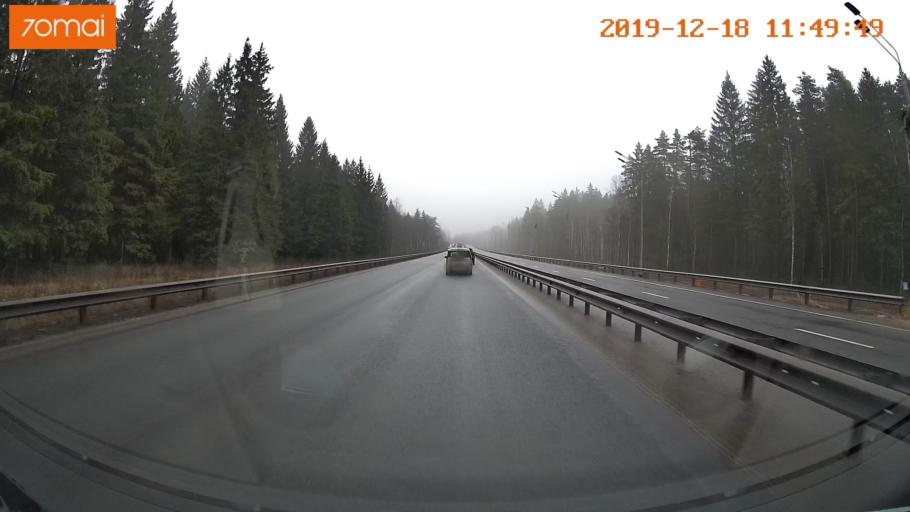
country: RU
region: Moskovskaya
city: Yershovo
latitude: 55.7807
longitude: 36.9143
